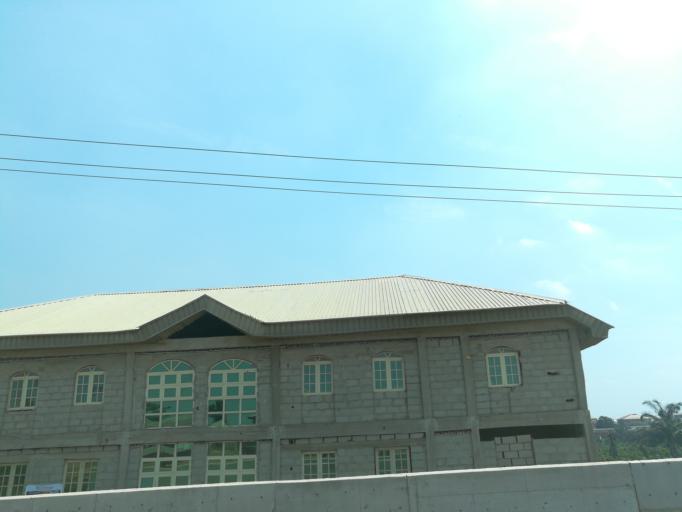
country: NG
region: Lagos
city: Ikorodu
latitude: 6.6611
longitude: 3.4707
